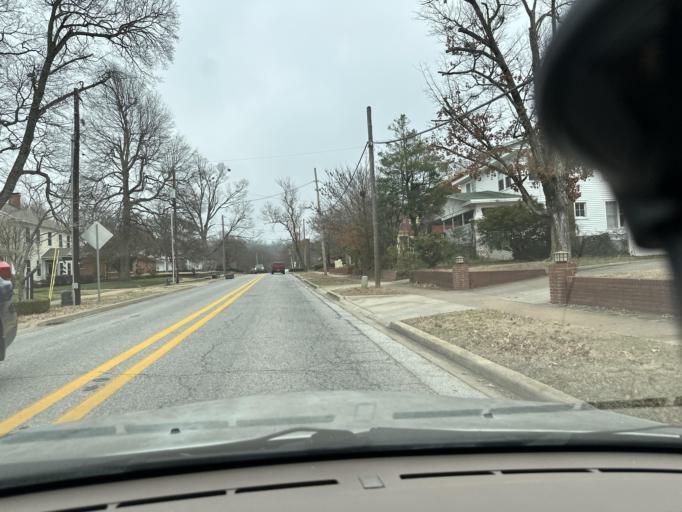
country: US
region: Arkansas
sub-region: Washington County
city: Fayetteville
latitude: 36.0685
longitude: -94.1559
